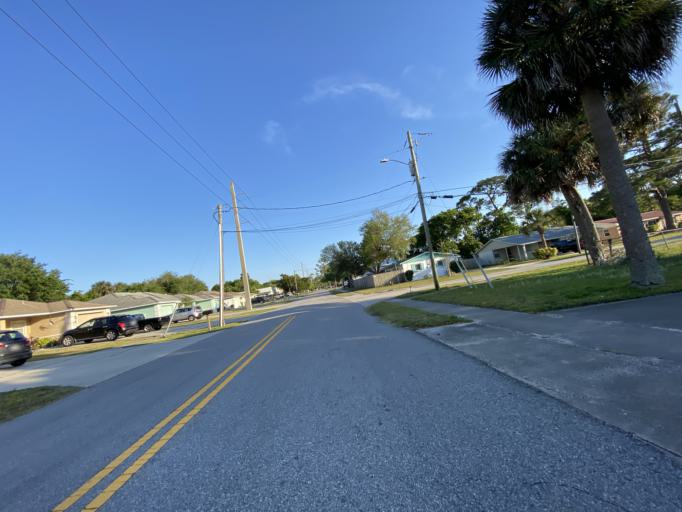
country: US
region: Florida
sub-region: Volusia County
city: South Daytona
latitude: 29.1718
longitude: -81.0071
